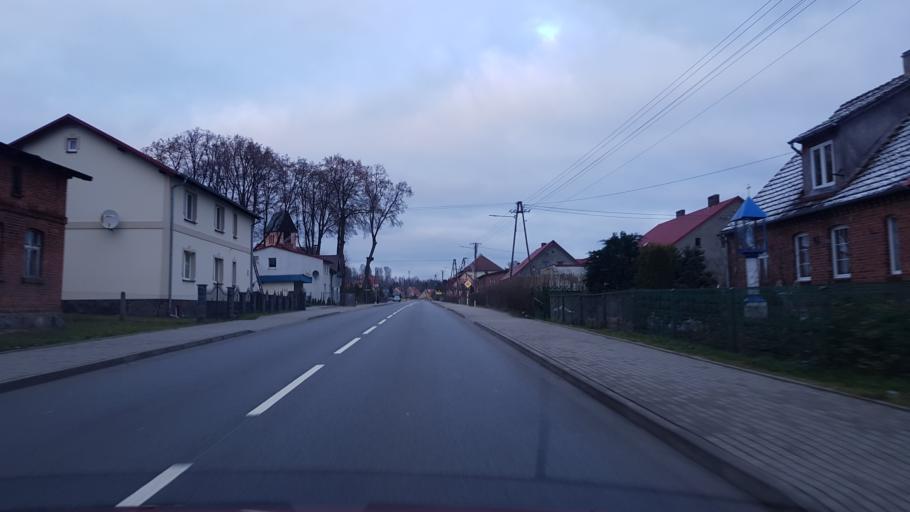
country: PL
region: Pomeranian Voivodeship
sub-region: Powiat bytowski
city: Tuchomie
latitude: 54.0577
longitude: 17.2400
